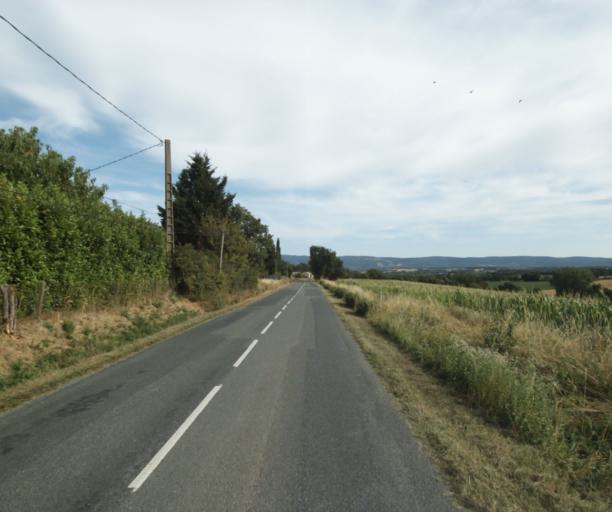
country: FR
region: Midi-Pyrenees
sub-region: Departement du Tarn
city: Soual
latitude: 43.5362
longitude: 2.0605
